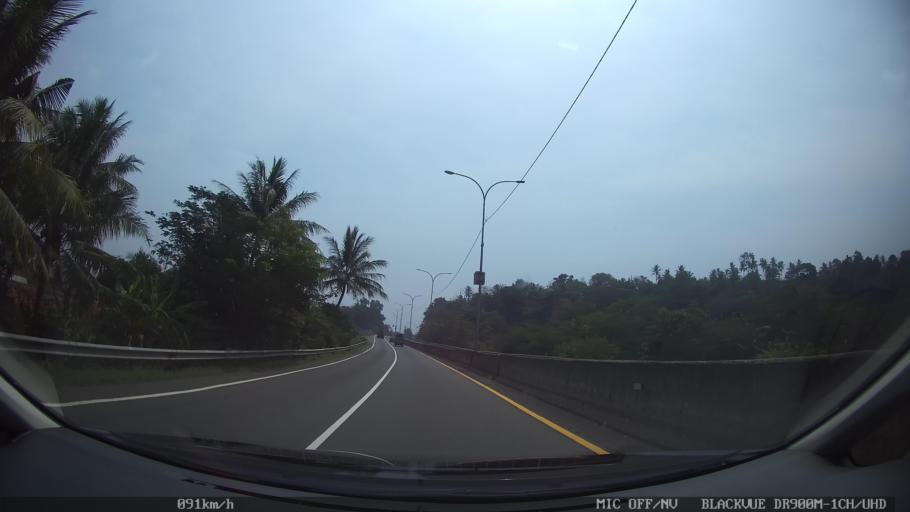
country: ID
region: Banten
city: Curug
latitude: -5.9785
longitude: 106.0171
